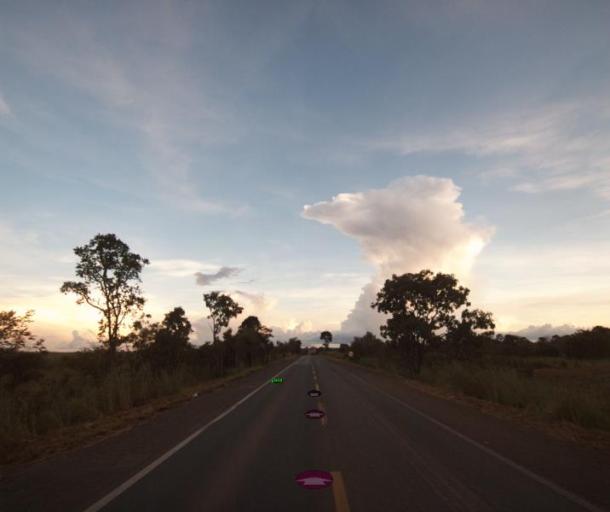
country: BR
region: Goias
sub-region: Uruacu
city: Uruacu
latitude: -14.4372
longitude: -49.1568
